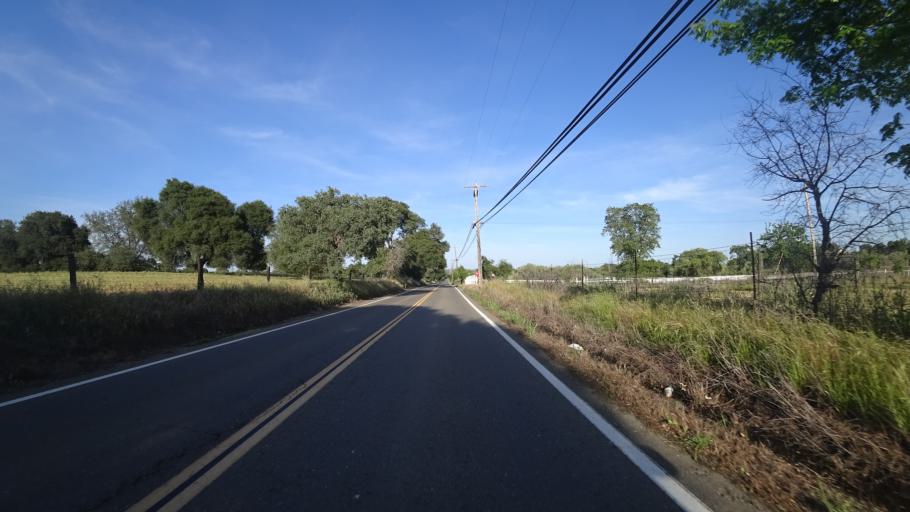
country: US
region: California
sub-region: Placer County
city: Lincoln
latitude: 38.9266
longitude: -121.2386
